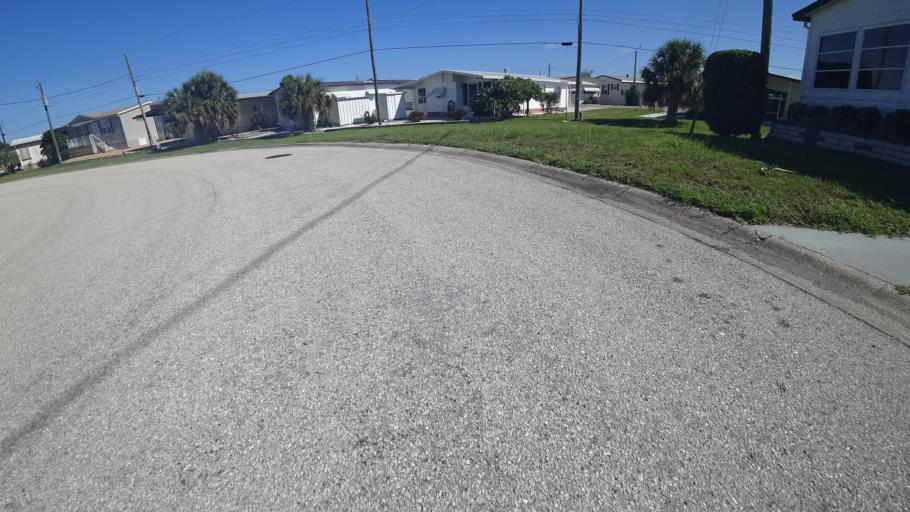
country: US
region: Florida
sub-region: Manatee County
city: Bayshore Gardens
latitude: 27.4201
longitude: -82.5829
